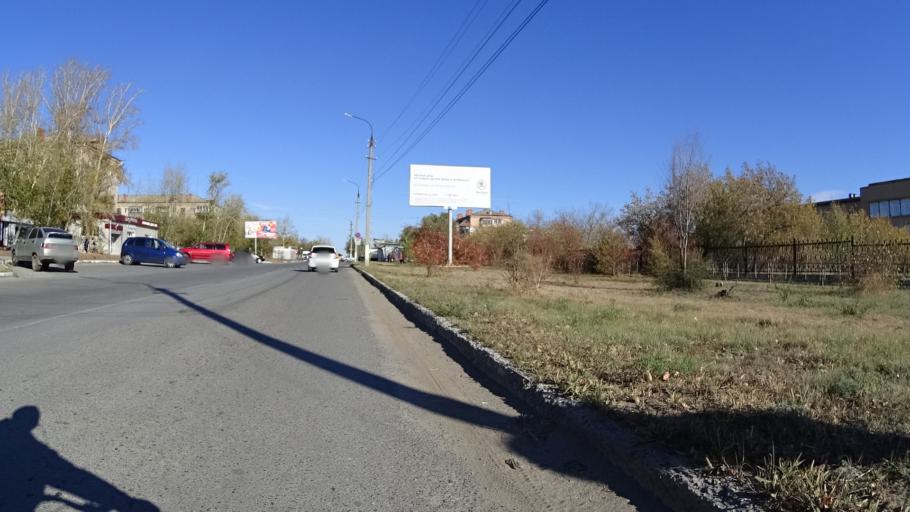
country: RU
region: Chelyabinsk
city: Troitsk
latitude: 54.0774
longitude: 61.5314
